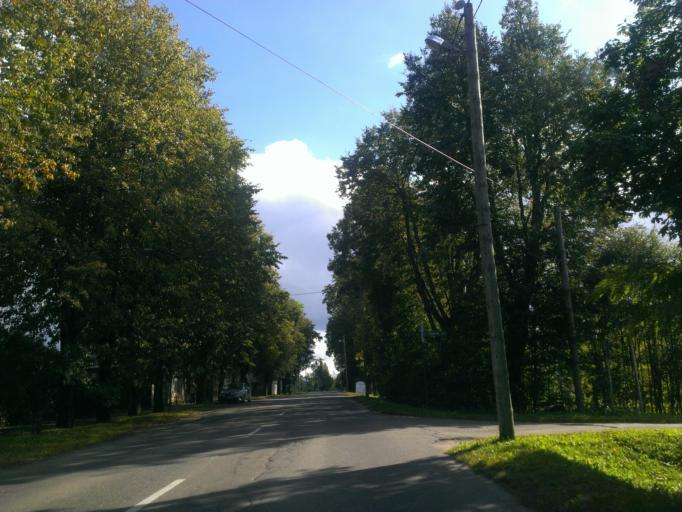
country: LV
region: Sigulda
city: Sigulda
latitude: 57.1499
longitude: 24.8548
